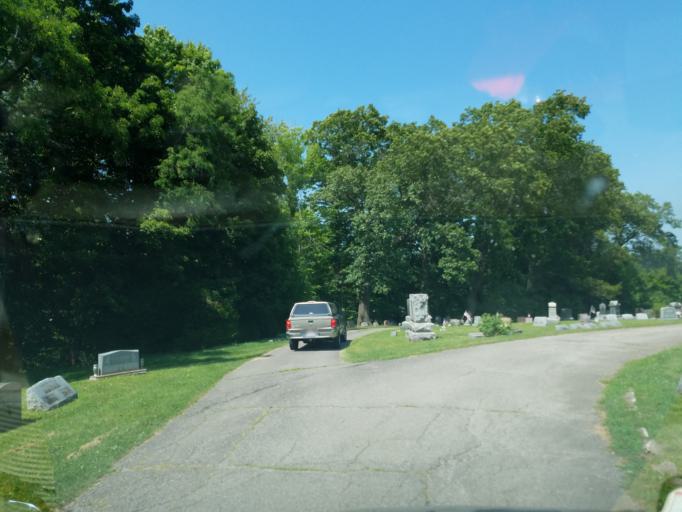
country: US
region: Ohio
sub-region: Ashland County
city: Ashland
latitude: 40.8665
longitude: -82.3271
